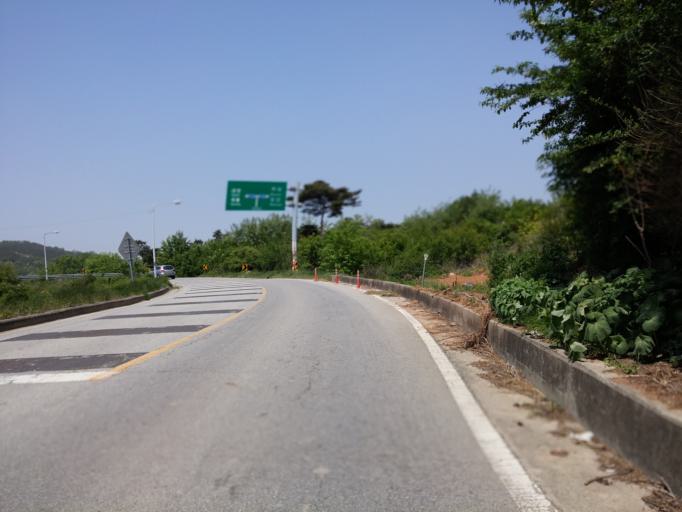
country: KR
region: Chungcheongnam-do
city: Nonsan
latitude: 36.2131
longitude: 127.1803
